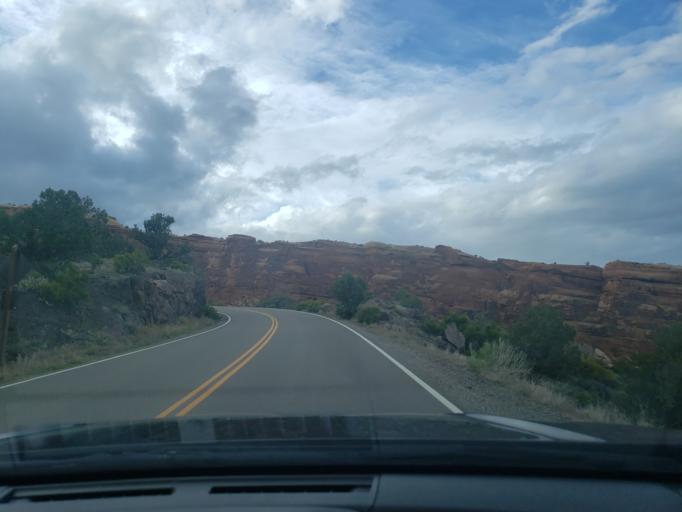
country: US
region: Colorado
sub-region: Mesa County
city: Redlands
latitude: 39.0269
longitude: -108.6383
